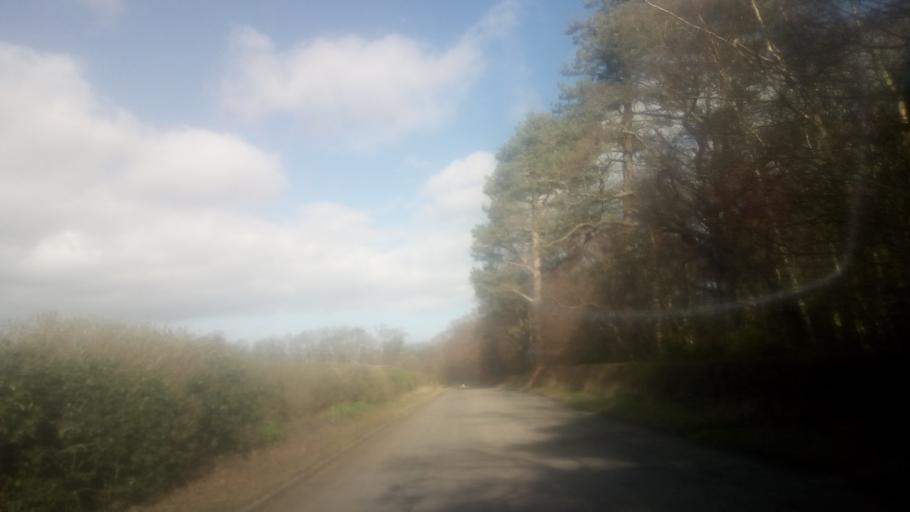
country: GB
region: Scotland
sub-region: Fife
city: Pathhead
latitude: 55.8830
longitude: -2.9595
